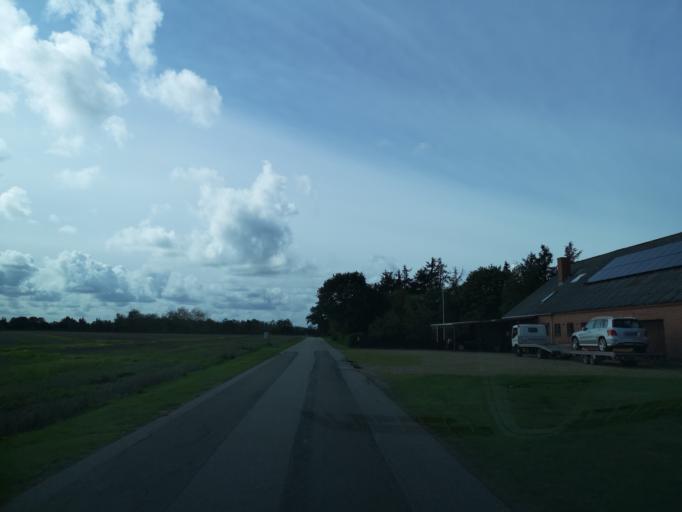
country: DK
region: Central Jutland
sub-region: Ringkobing-Skjern Kommune
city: Skjern
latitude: 55.9469
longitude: 8.5370
